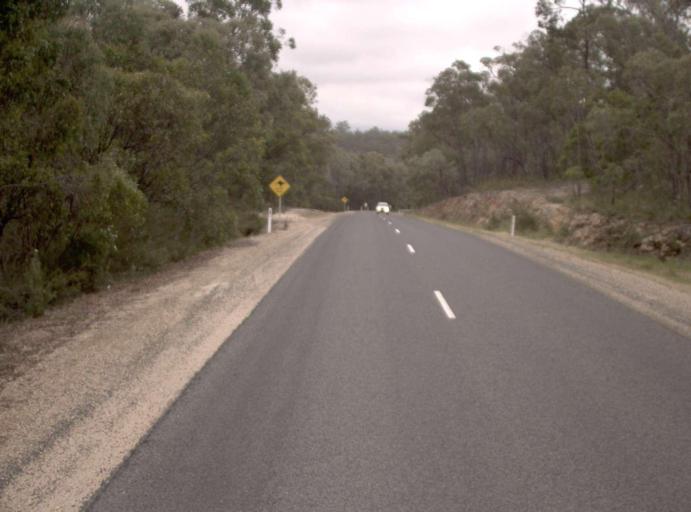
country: AU
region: Victoria
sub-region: Wellington
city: Heyfield
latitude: -37.9313
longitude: 146.7570
